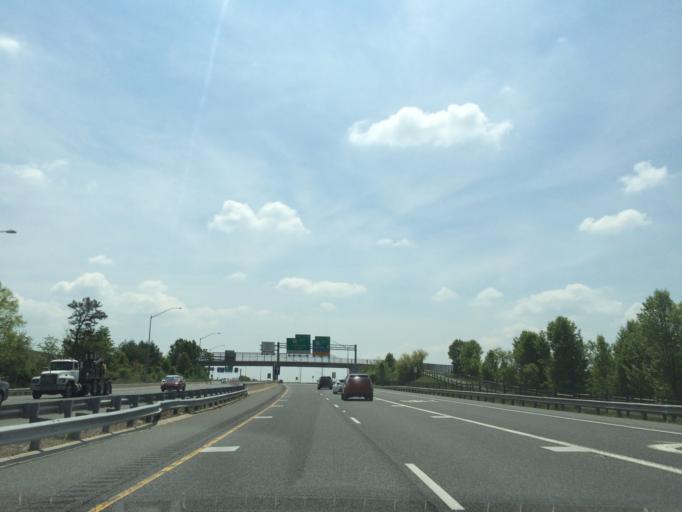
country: US
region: Maryland
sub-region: Howard County
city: Elkridge
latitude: 39.1922
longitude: -76.6876
